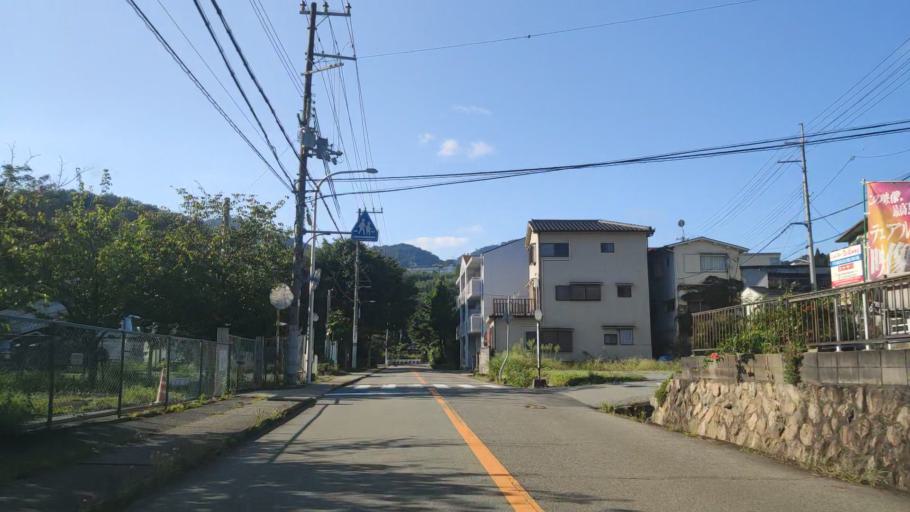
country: JP
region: Hyogo
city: Sandacho
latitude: 34.8057
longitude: 135.2496
